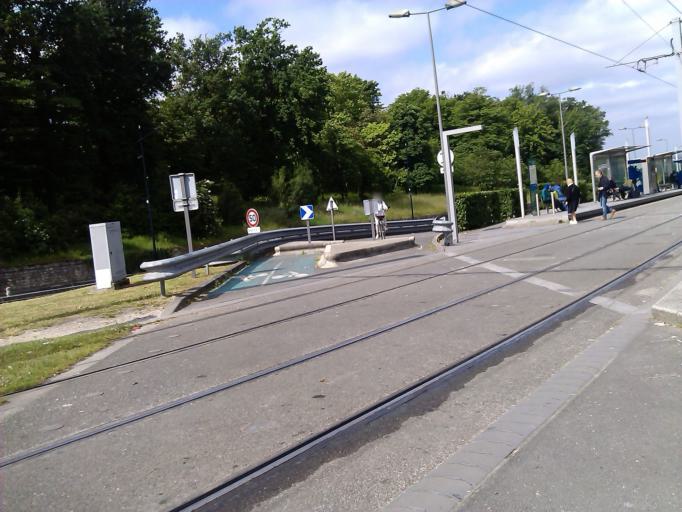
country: FR
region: Aquitaine
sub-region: Departement de la Gironde
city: Cenon
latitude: 44.8643
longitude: -0.5241
